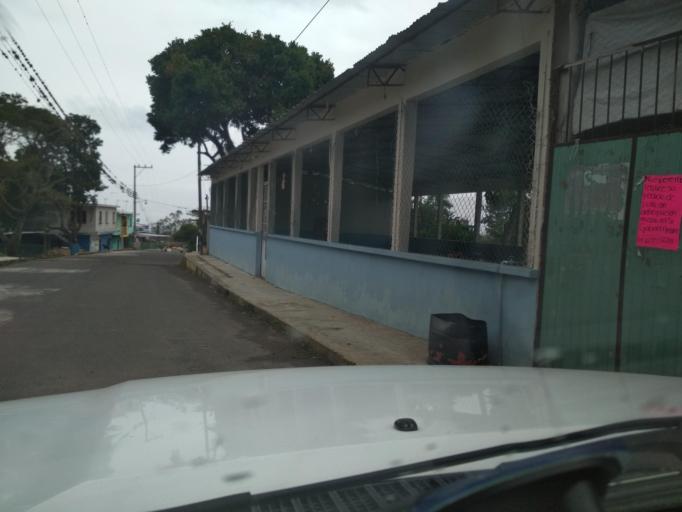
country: MX
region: Veracruz
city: El Castillo
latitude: 19.5360
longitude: -96.8172
